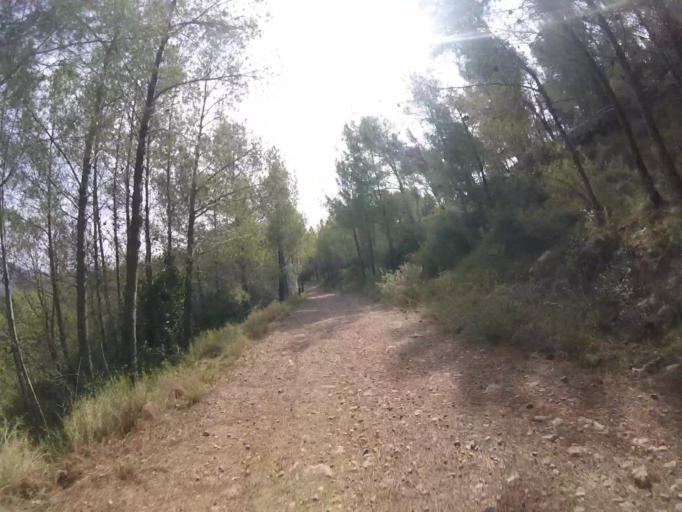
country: ES
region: Valencia
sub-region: Provincia de Castello
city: Benicassim
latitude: 40.0852
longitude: 0.0502
